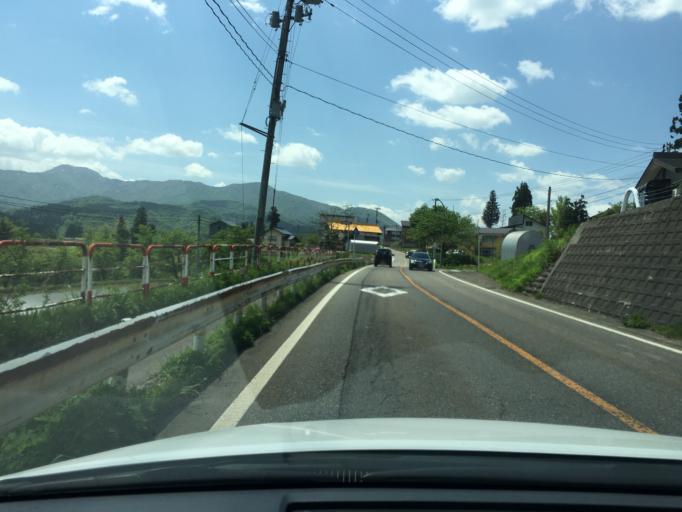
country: JP
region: Niigata
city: Tochio-honcho
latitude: 37.3318
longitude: 139.0273
